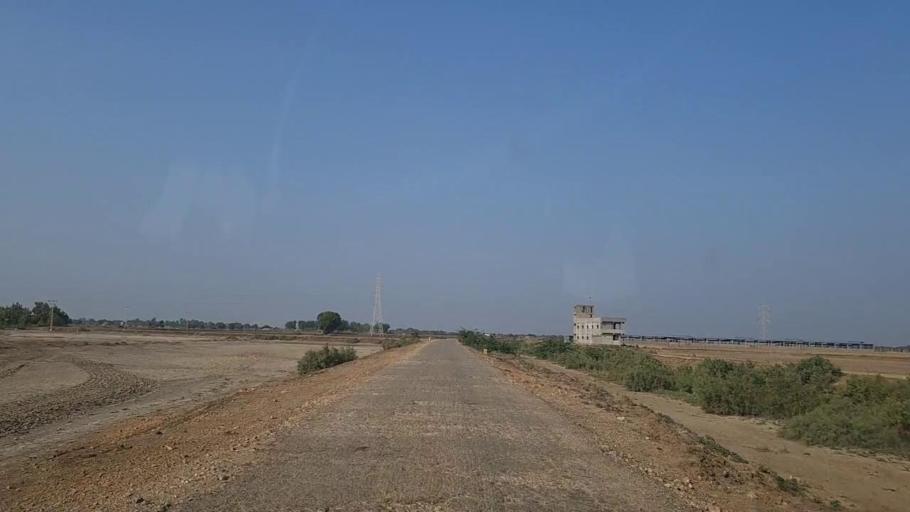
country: PK
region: Sindh
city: Mirpur Sakro
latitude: 24.5610
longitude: 67.6708
